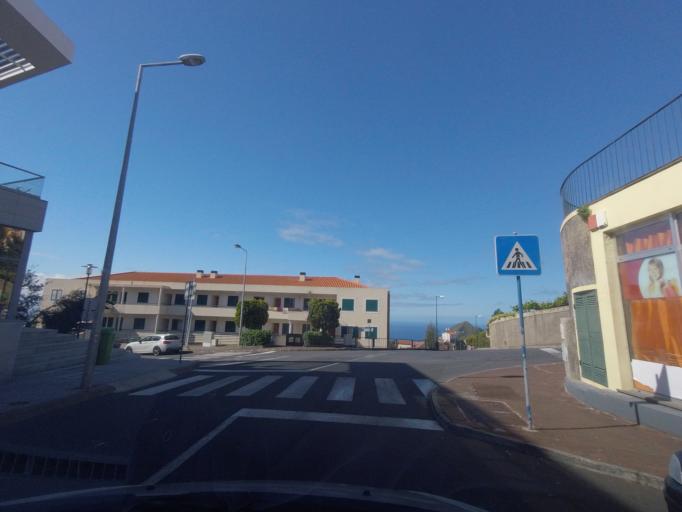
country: PT
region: Madeira
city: Camara de Lobos
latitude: 32.6696
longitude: -16.9774
